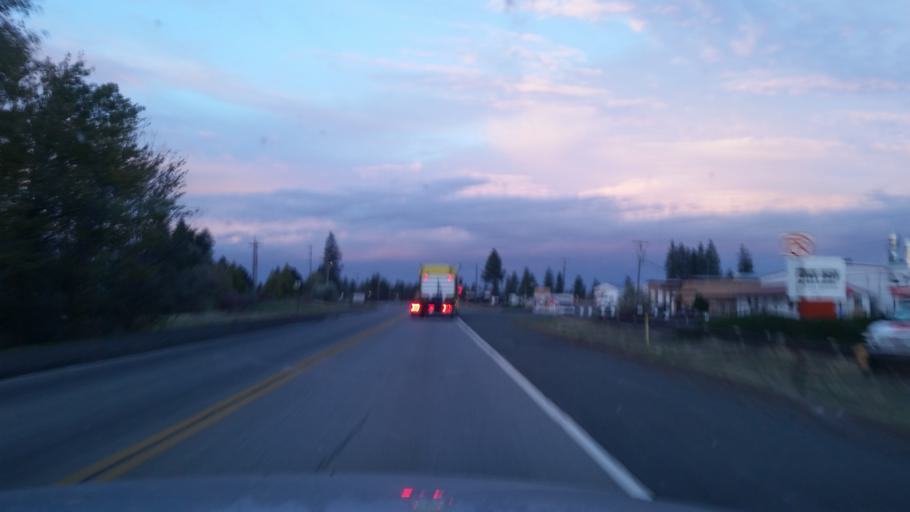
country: US
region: Washington
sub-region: Spokane County
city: Spokane
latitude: 47.6260
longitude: -117.5020
